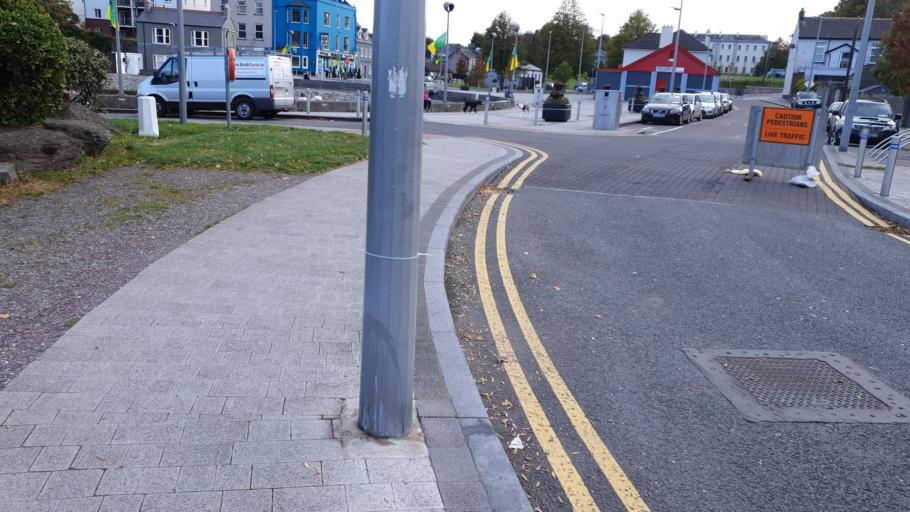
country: IE
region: Munster
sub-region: County Cork
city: Cork
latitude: 51.8982
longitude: -8.4137
